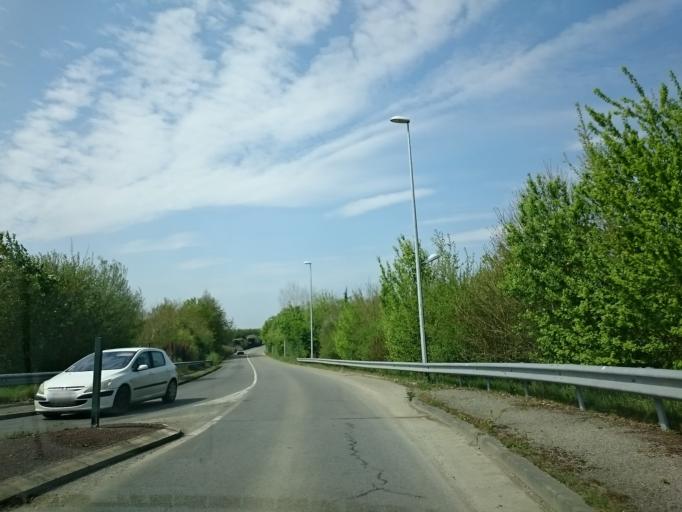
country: FR
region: Brittany
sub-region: Departement d'Ille-et-Vilaine
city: Vern-sur-Seiche
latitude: 48.0358
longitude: -1.5999
